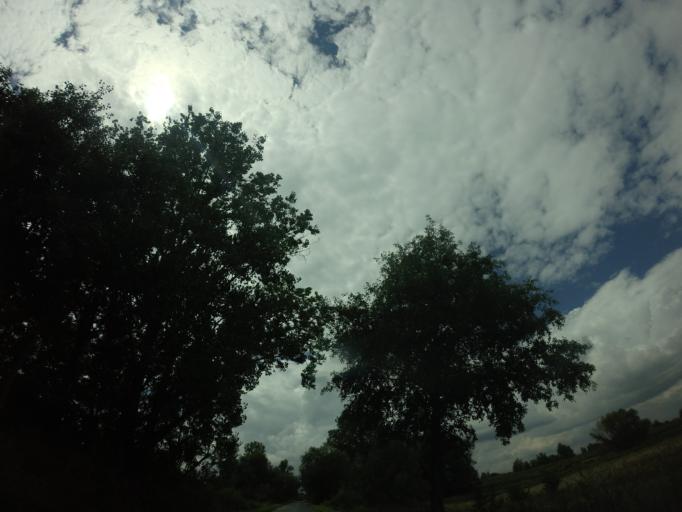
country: PL
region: Lublin Voivodeship
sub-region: Powiat opolski
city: Wilkow
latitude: 51.2661
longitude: 21.8924
